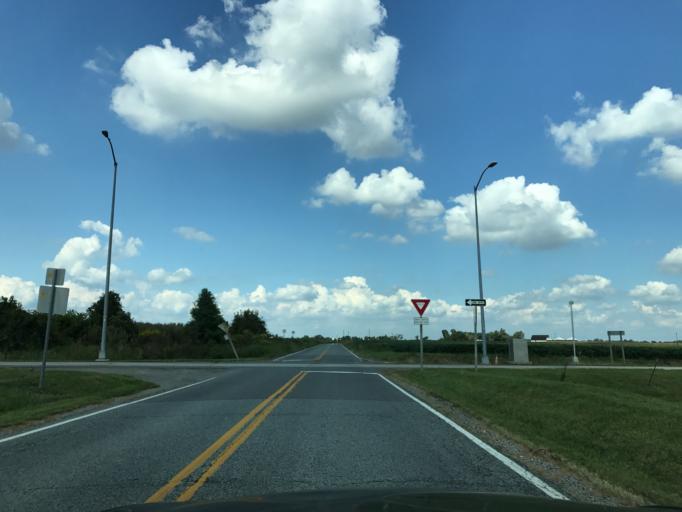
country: US
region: Delaware
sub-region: New Castle County
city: Middletown
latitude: 39.3852
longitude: -75.7998
